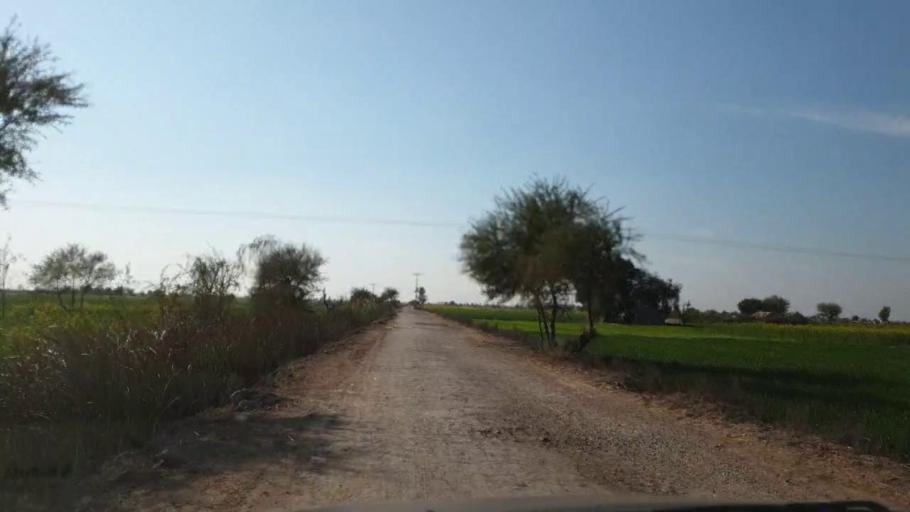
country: PK
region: Sindh
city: Khadro
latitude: 26.1552
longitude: 68.7613
